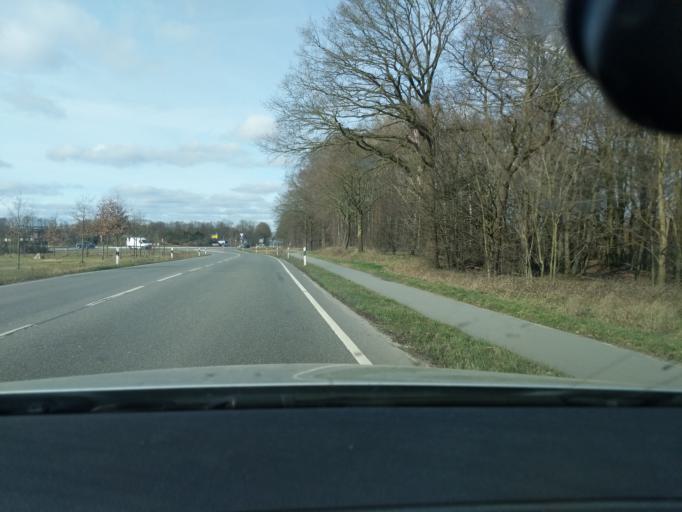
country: DE
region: Lower Saxony
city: Agathenburg
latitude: 53.5694
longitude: 9.5206
